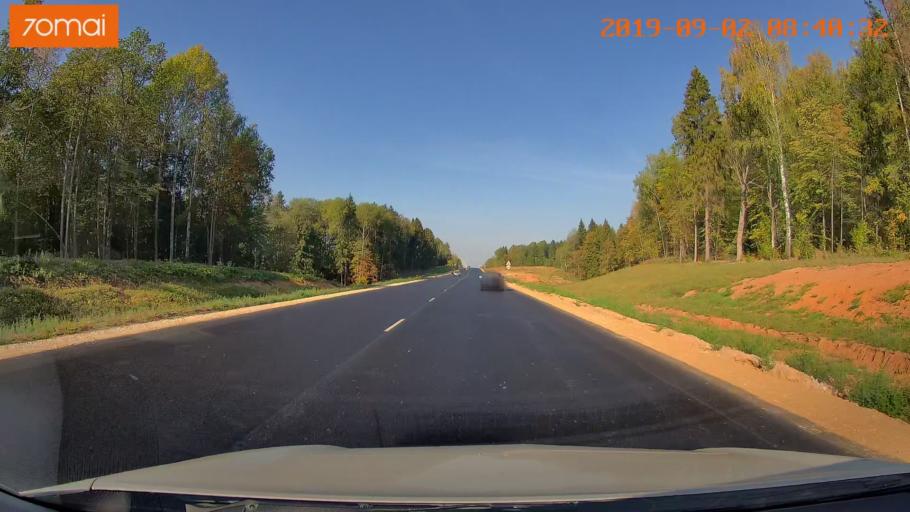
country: RU
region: Kaluga
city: Kudinovo
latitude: 54.9740
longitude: 36.1317
